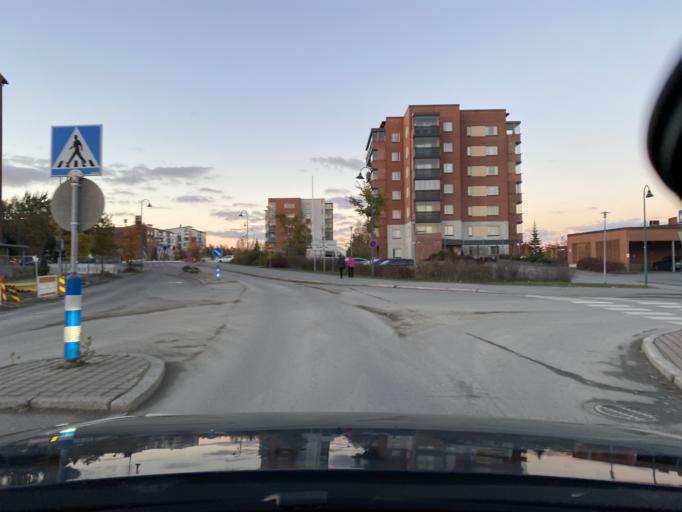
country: FI
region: Pirkanmaa
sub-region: Tampere
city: Lempaeaelae
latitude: 61.3139
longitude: 23.7587
